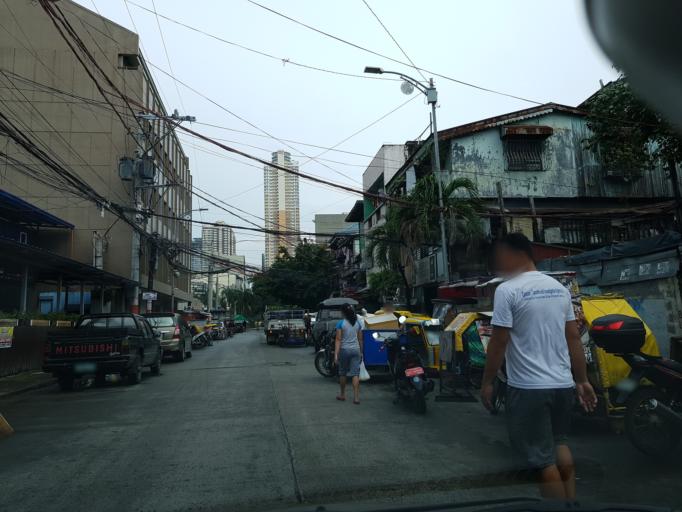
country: PH
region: Metro Manila
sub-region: City of Manila
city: Port Area
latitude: 14.5694
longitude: 120.9872
